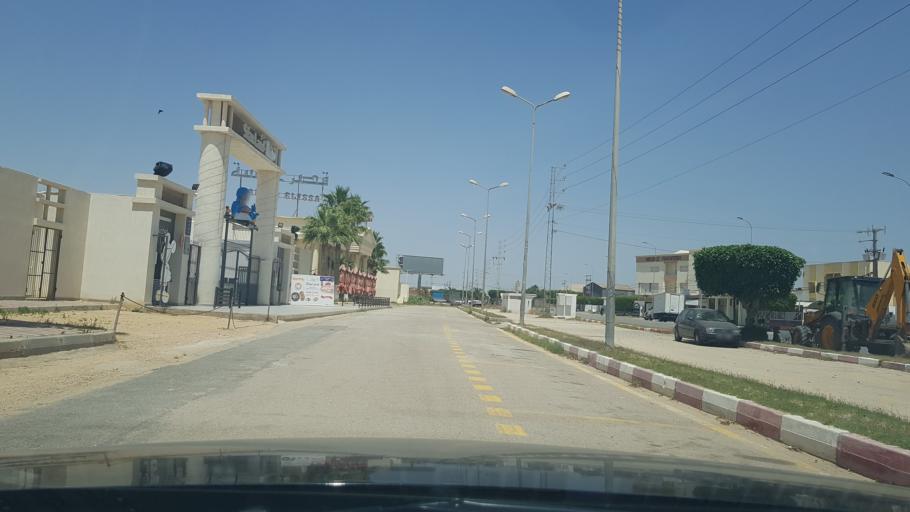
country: TN
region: Safaqis
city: Al Qarmadah
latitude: 34.8435
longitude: 10.7625
